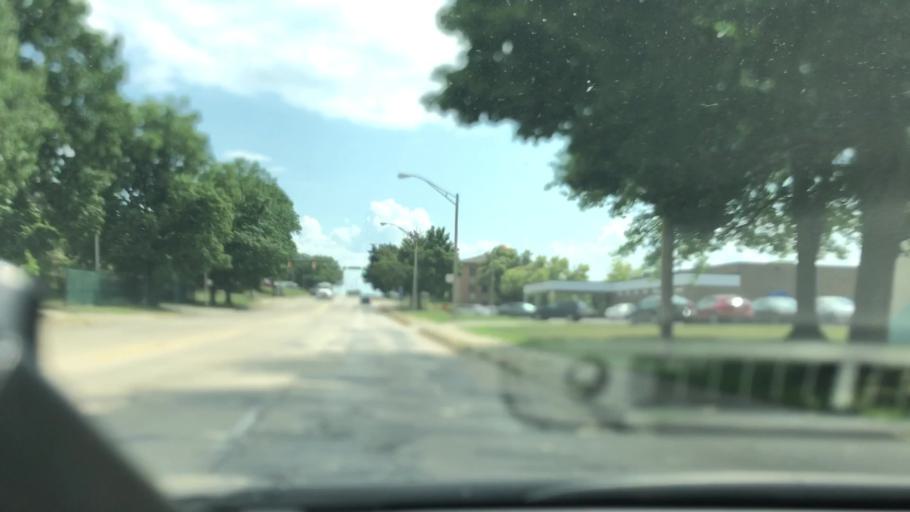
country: US
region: Ohio
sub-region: Summit County
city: Akron
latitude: 41.0672
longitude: -81.5205
